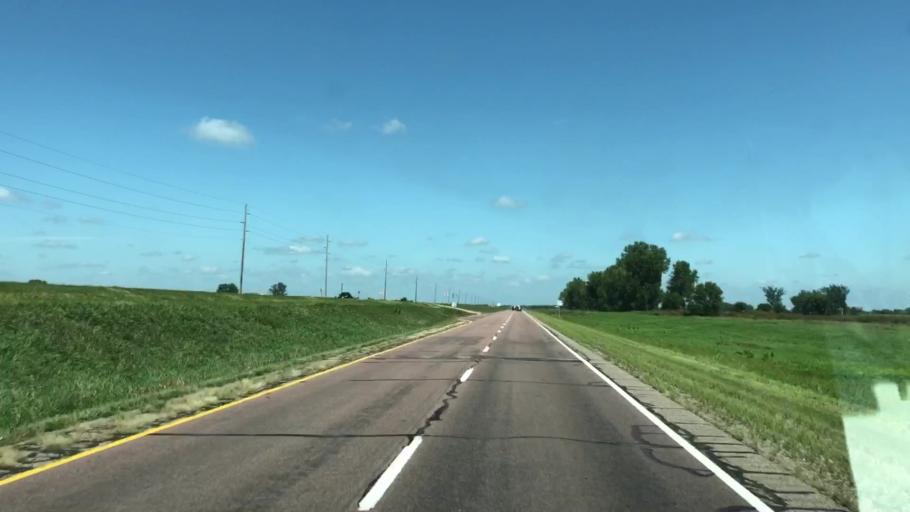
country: US
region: Iowa
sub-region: Plymouth County
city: Le Mars
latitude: 42.6762
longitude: -96.2708
